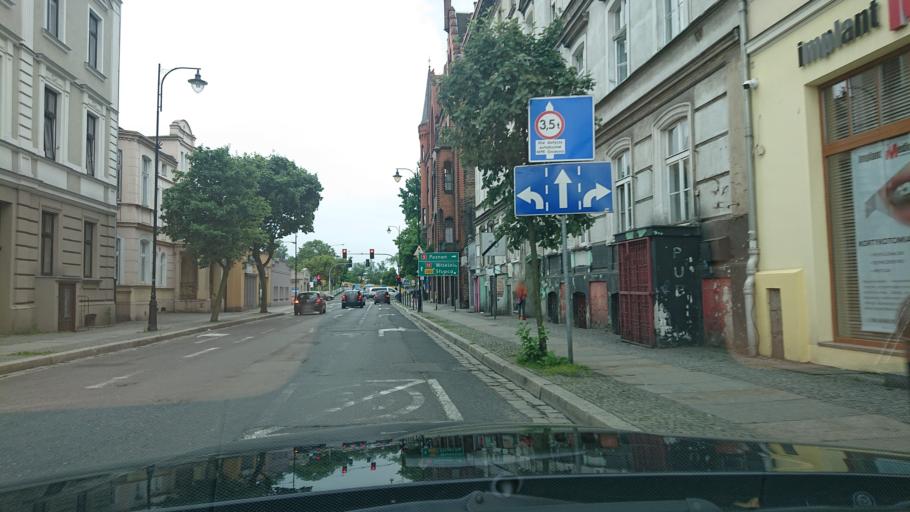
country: PL
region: Greater Poland Voivodeship
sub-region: Powiat gnieznienski
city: Gniezno
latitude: 52.5317
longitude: 17.5965
